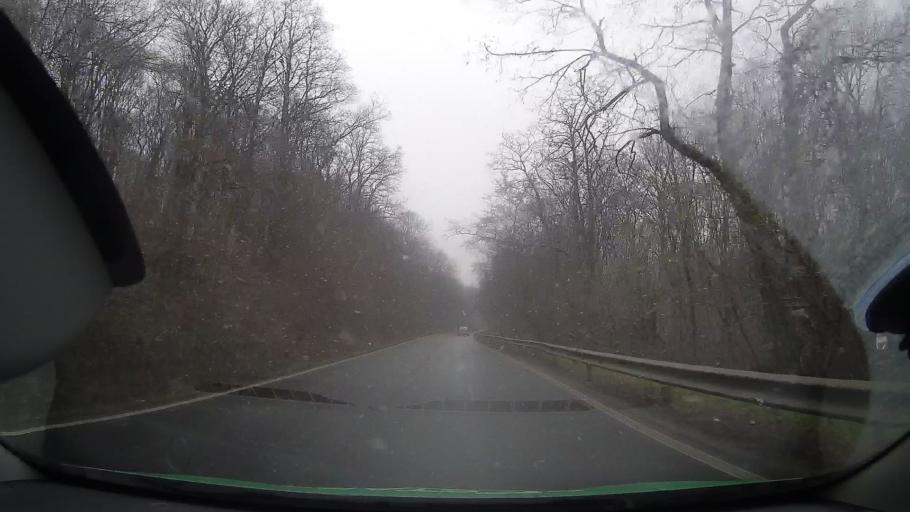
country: RO
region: Sibiu
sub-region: Comuna Blajel
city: Blajel
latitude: 46.1874
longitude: 24.3258
